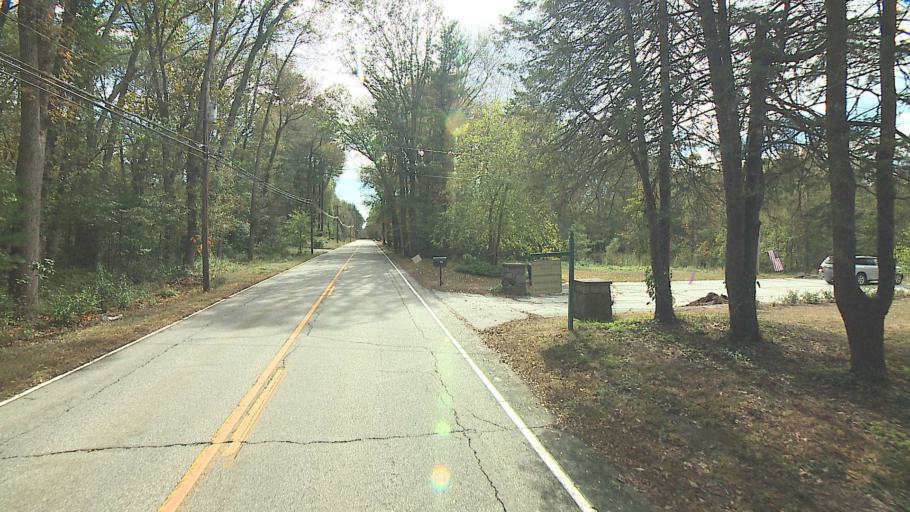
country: US
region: Connecticut
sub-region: Windham County
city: Killingly Center
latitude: 41.8821
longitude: -71.8749
